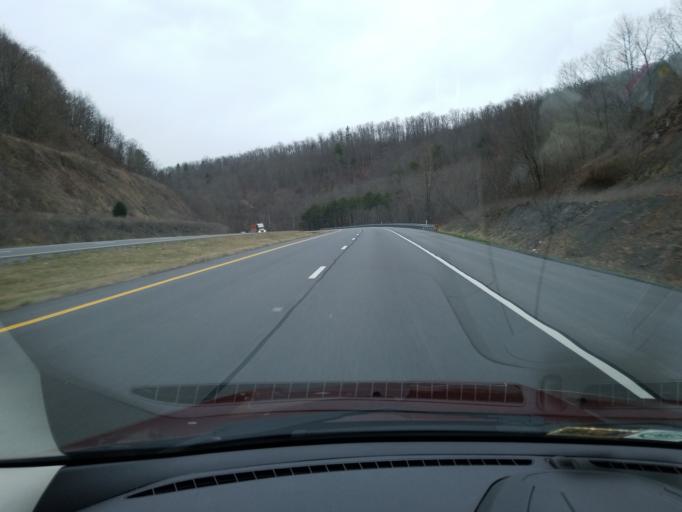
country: US
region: West Virginia
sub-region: Mercer County
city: Athens
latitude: 37.3459
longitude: -80.9409
